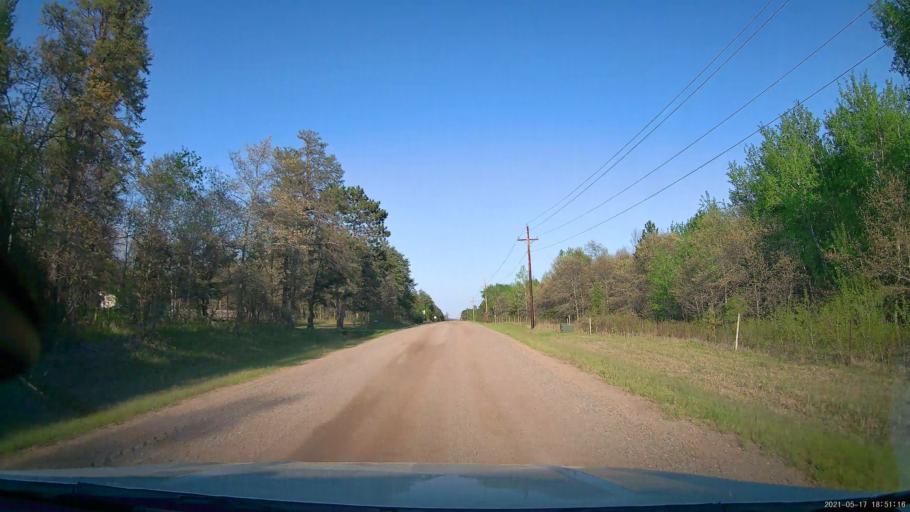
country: US
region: Minnesota
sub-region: Hubbard County
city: Park Rapids
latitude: 46.9437
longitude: -95.0148
